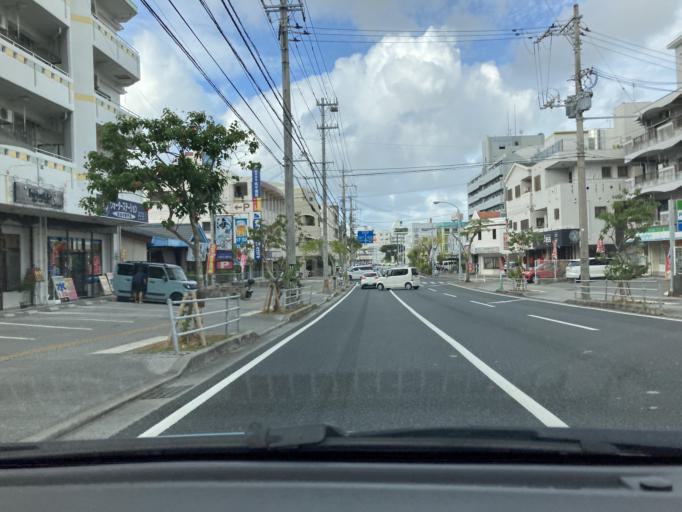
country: JP
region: Okinawa
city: Tomigusuku
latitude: 26.1921
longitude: 127.6754
